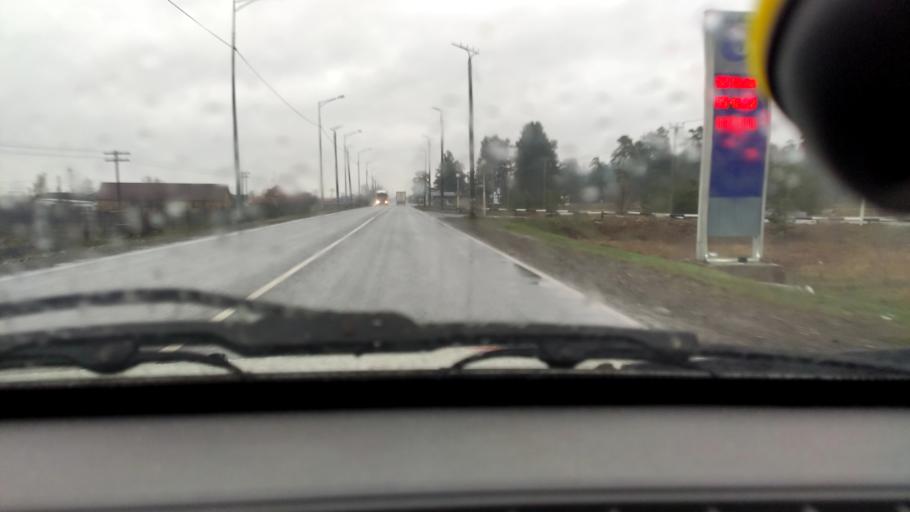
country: RU
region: Samara
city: Povolzhskiy
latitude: 53.5831
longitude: 49.5683
